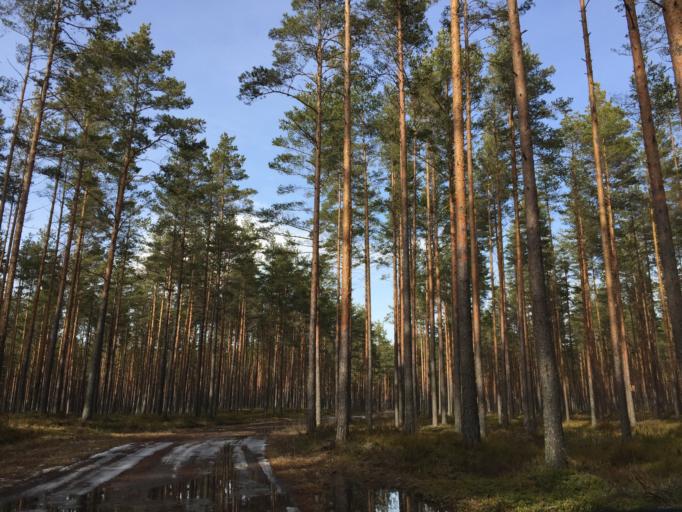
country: EE
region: Paernumaa
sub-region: Paernu linn
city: Parnu
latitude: 58.2369
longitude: 24.5199
